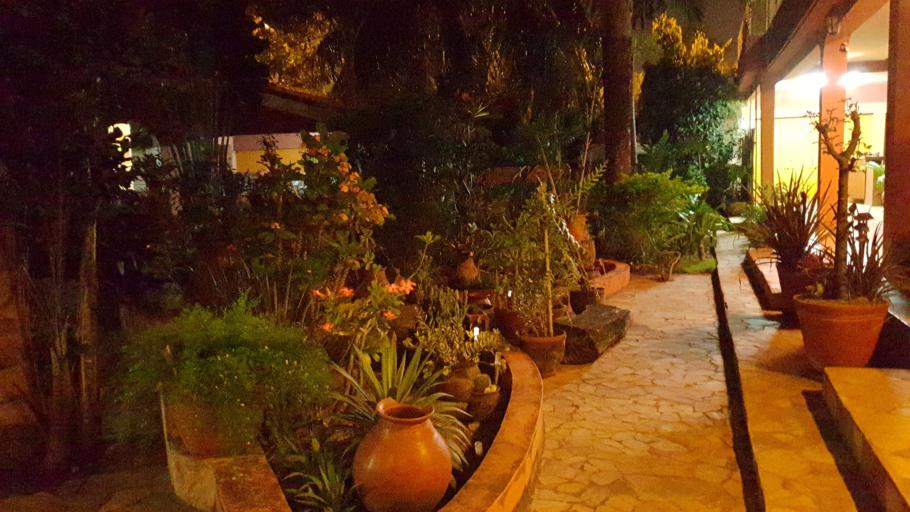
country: TG
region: Maritime
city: Lome
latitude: 6.2059
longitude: 1.1915
